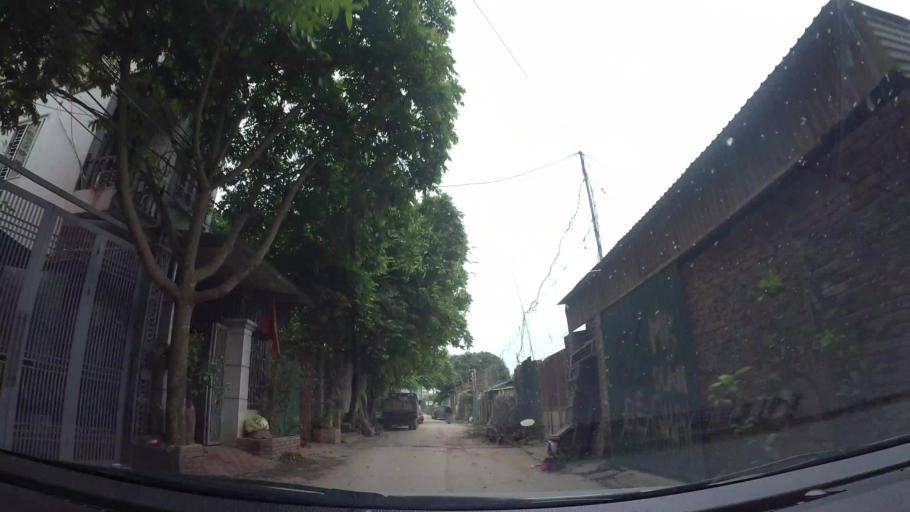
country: VN
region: Ha Noi
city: Tay Ho
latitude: 21.0645
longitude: 105.8376
